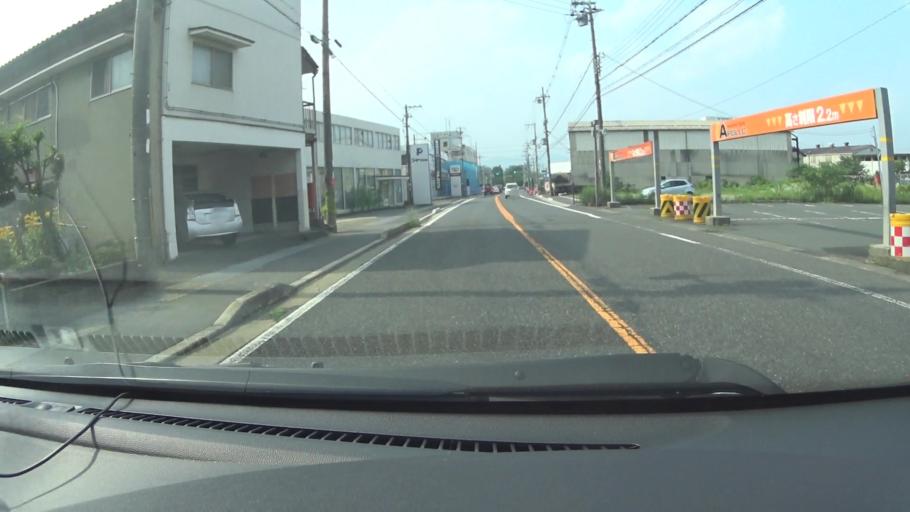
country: JP
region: Kyoto
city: Maizuru
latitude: 35.4518
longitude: 135.3468
